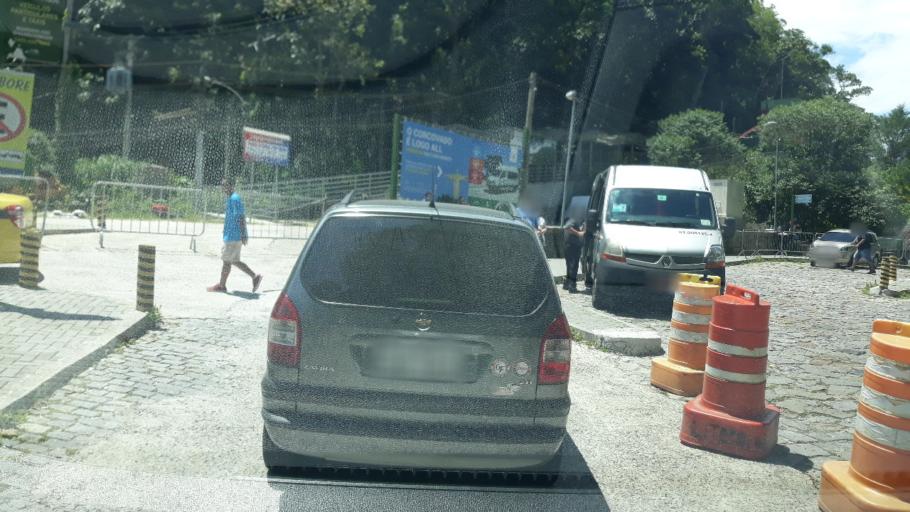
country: BR
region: Rio de Janeiro
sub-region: Rio De Janeiro
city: Rio de Janeiro
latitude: -22.9462
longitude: -43.2177
